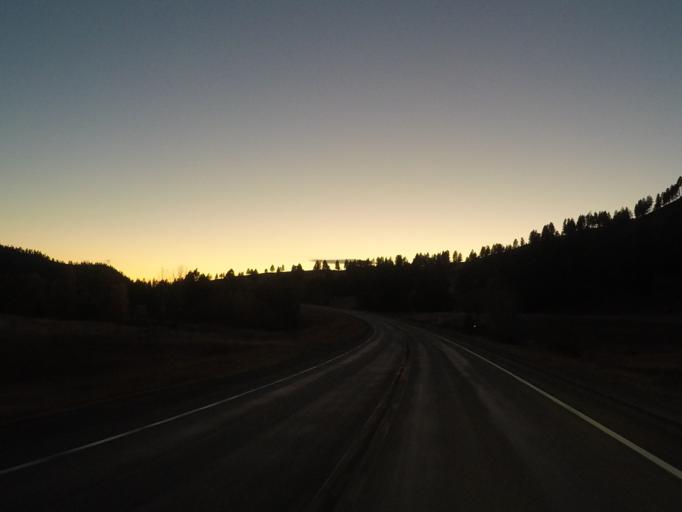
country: US
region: Montana
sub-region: Missoula County
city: Seeley Lake
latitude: 47.0301
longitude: -113.2780
